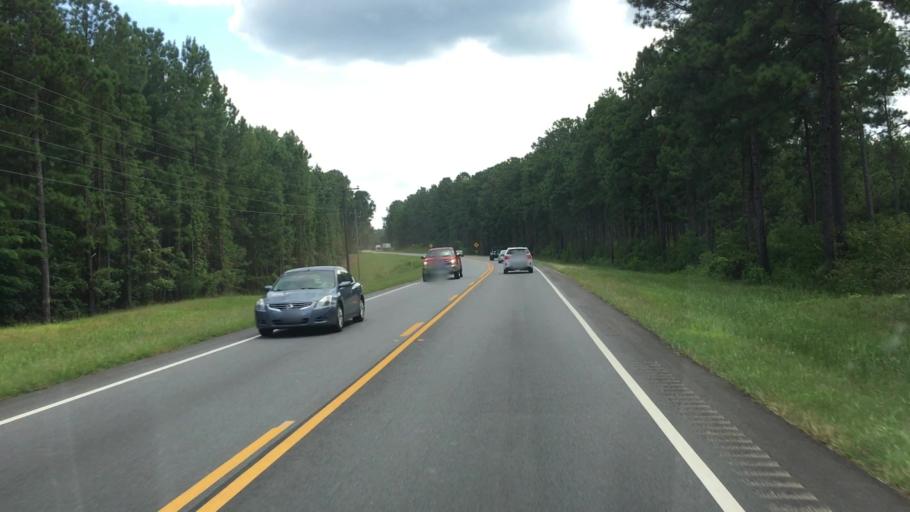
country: US
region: Georgia
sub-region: Putnam County
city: Jefferson
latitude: 33.4003
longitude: -83.3686
